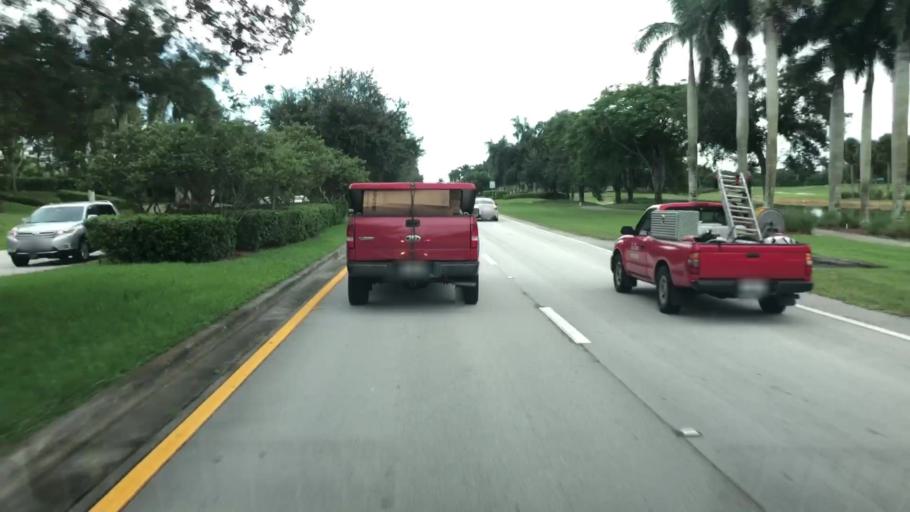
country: US
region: Florida
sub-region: Broward County
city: Parkland
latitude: 26.3128
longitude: -80.2790
